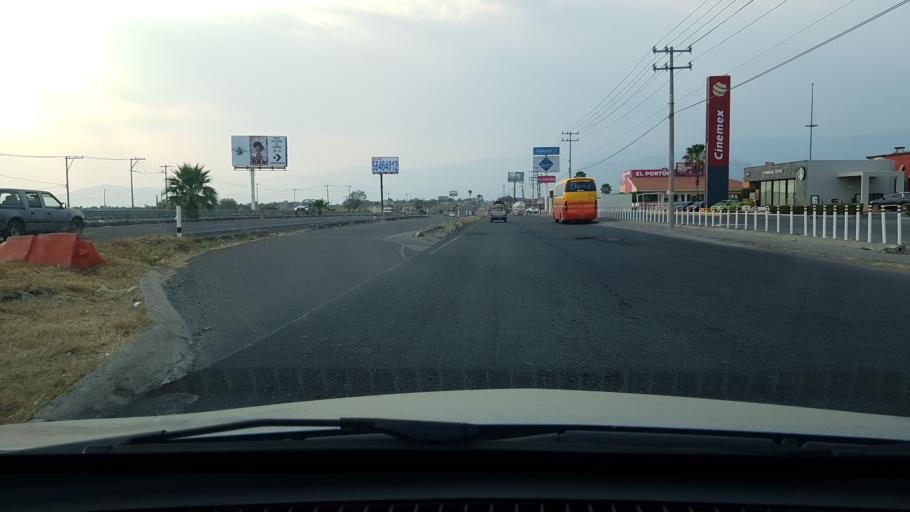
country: MX
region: Morelos
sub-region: Cuautla
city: Tierra Larga (Campo Nuevo)
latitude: 18.8666
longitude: -98.9510
